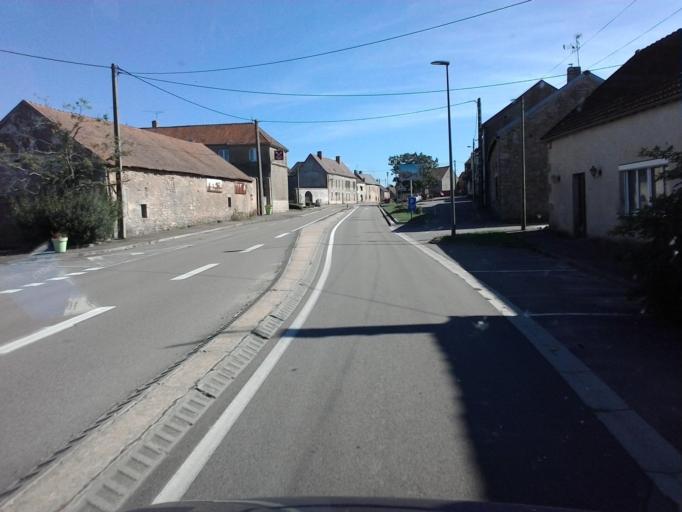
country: FR
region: Bourgogne
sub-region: Departement de la Cote-d'Or
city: Saulieu
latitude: 47.3829
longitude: 4.1764
